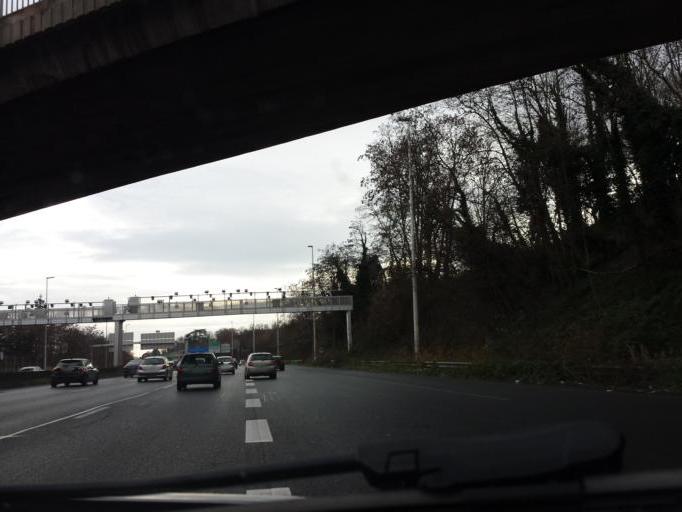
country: FR
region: Ile-de-France
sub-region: Departement du Val-d'Oise
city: Sannois
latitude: 48.9710
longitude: 2.2488
